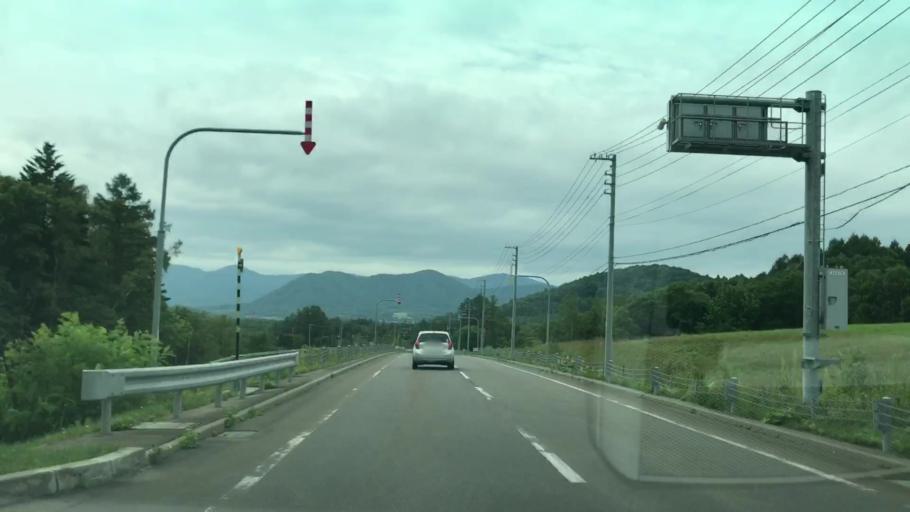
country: JP
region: Hokkaido
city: Yoichi
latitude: 43.1137
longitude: 140.8204
